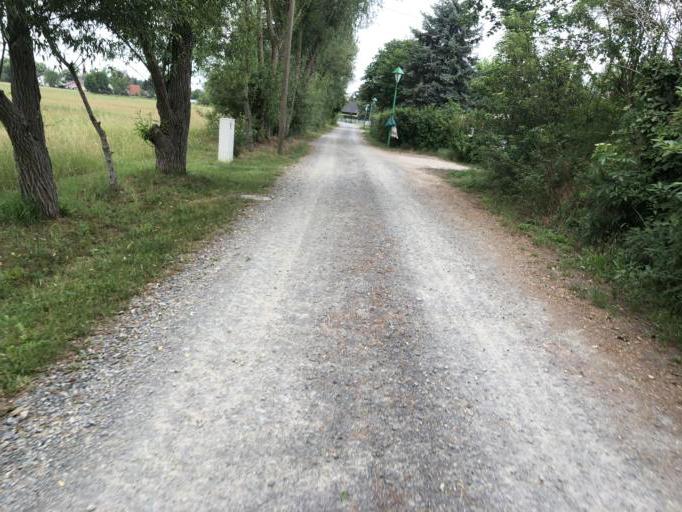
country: DE
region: Brandenburg
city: Bestensee
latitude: 52.2359
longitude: 13.7130
